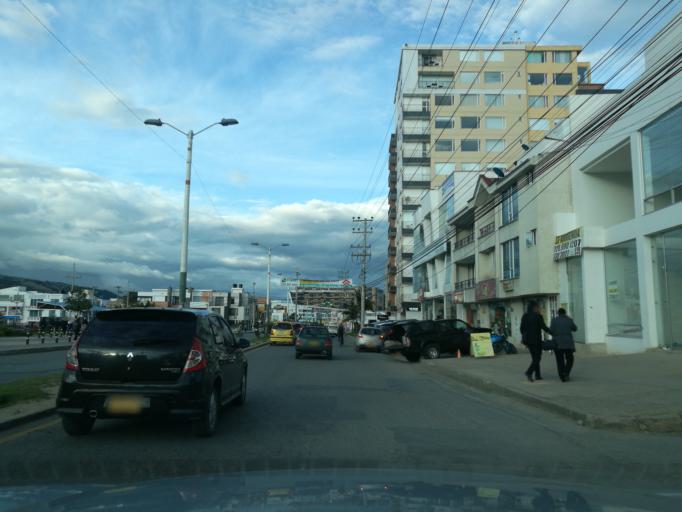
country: CO
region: Boyaca
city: Tunja
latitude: 5.5455
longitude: -73.3482
